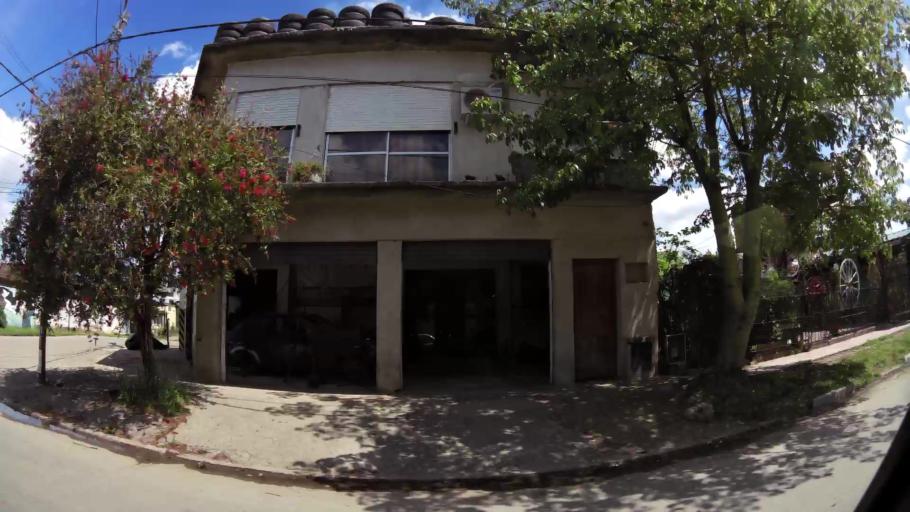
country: AR
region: Buenos Aires
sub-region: Partido de Quilmes
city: Quilmes
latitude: -34.8067
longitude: -58.2457
